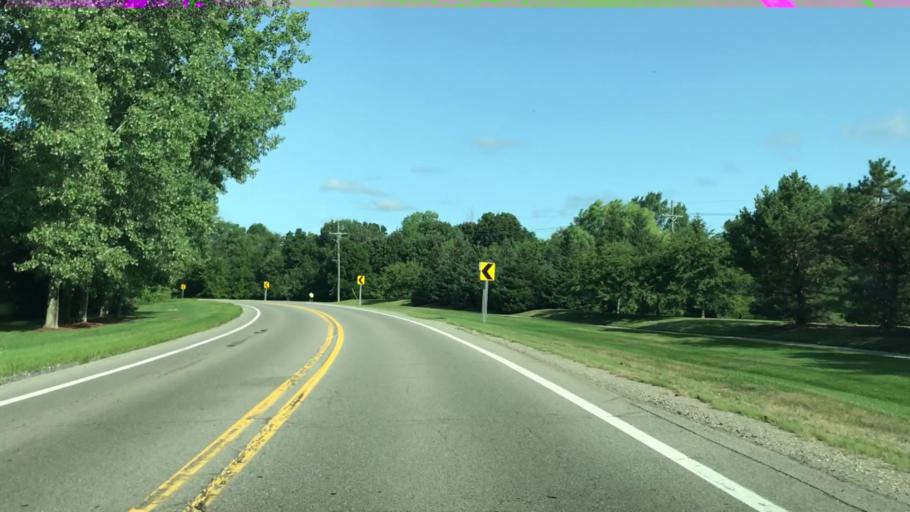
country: US
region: Michigan
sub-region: Oakland County
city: Rochester
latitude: 42.6846
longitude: -83.0987
